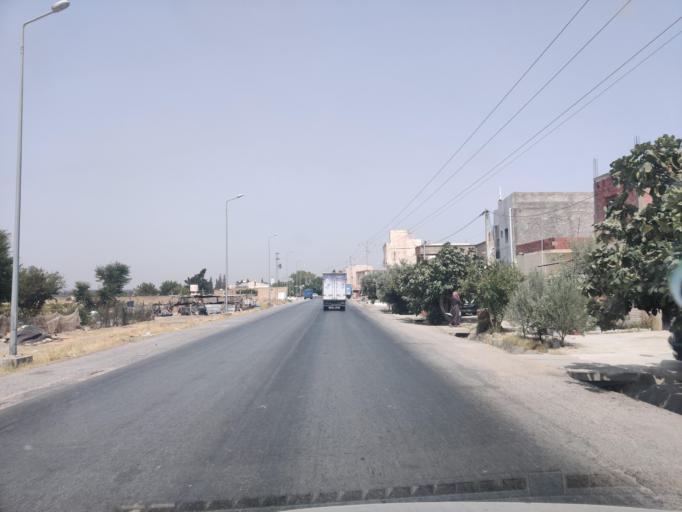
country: TN
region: Tunis
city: La Sebala du Mornag
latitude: 36.6587
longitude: 10.3297
